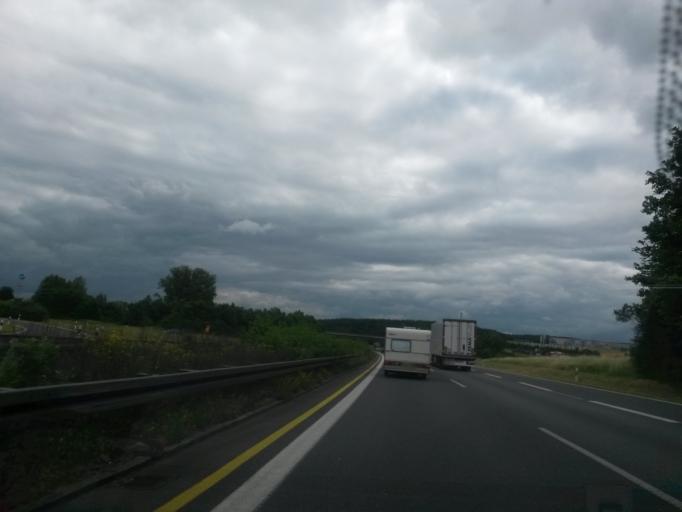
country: DE
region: Bavaria
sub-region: Upper Franconia
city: Schlusselfeld
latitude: 49.7453
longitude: 10.6287
